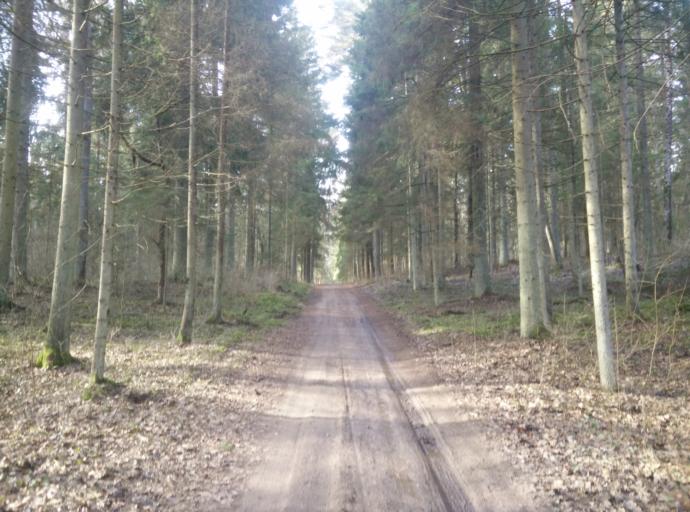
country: LT
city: Trakai
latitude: 54.6468
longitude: 24.9745
